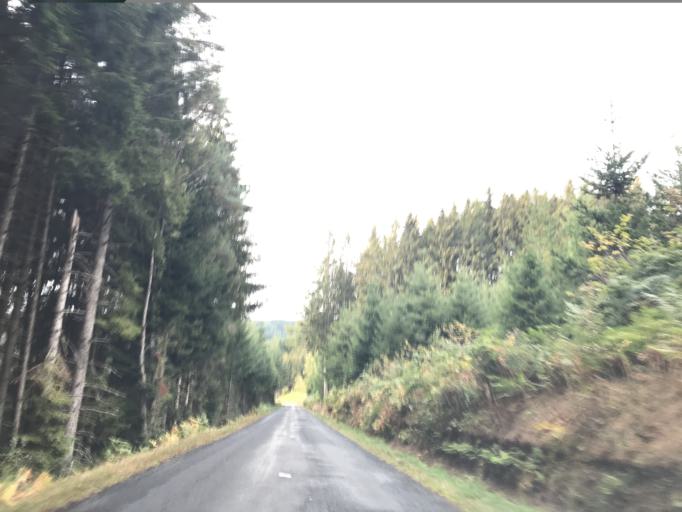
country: FR
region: Auvergne
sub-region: Departement du Puy-de-Dome
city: Celles-sur-Durolle
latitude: 45.7838
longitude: 3.6664
